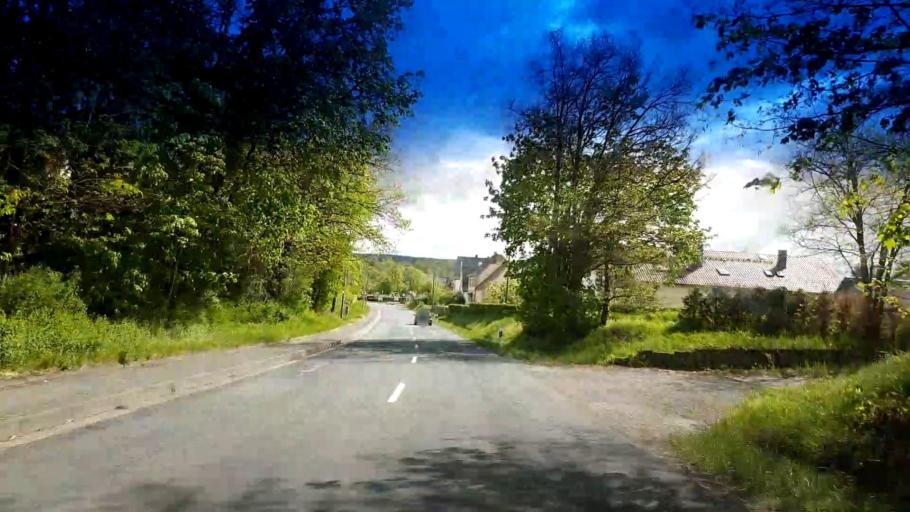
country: DE
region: Bavaria
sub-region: Upper Franconia
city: Frensdorf
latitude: 49.8258
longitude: 10.8408
